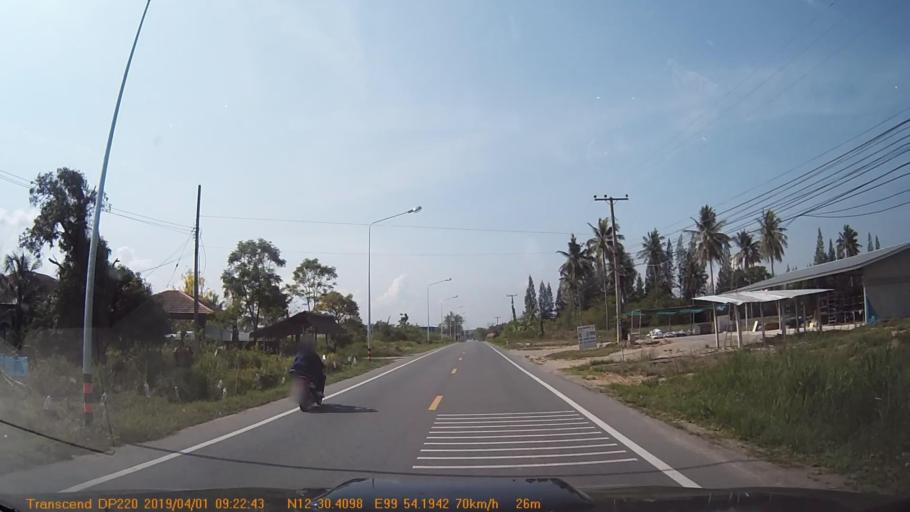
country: TH
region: Prachuap Khiri Khan
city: Hua Hin
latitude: 12.5064
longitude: 99.9033
